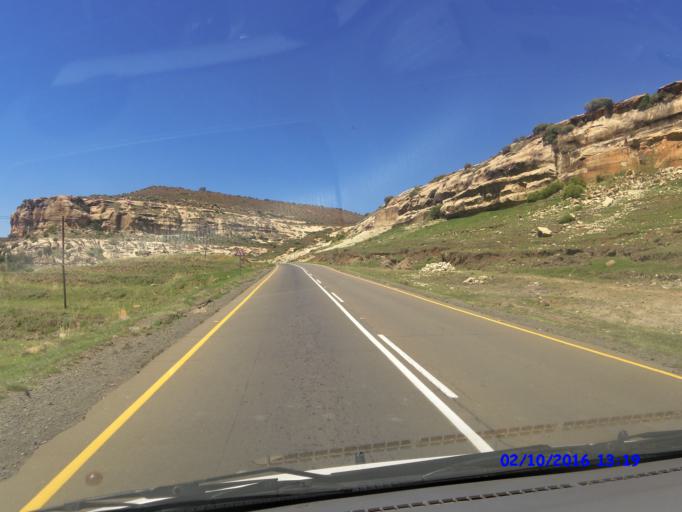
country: LS
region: Maseru
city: Nako
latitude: -29.4237
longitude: 27.6947
